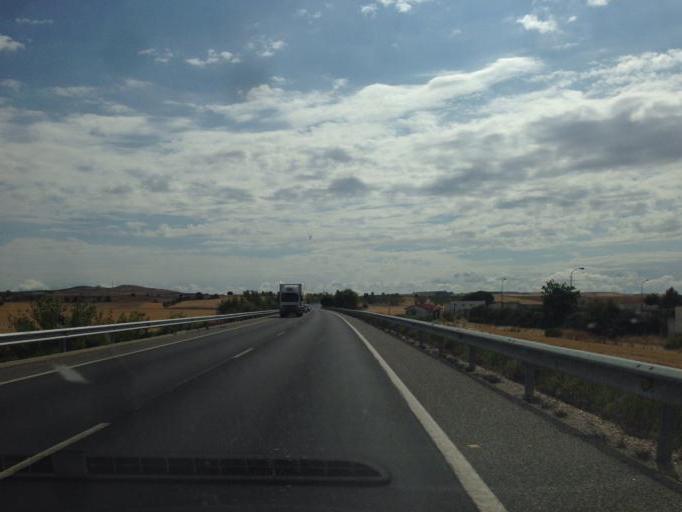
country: ES
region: Madrid
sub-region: Provincia de Madrid
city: Cobena
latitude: 40.5777
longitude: -3.5401
